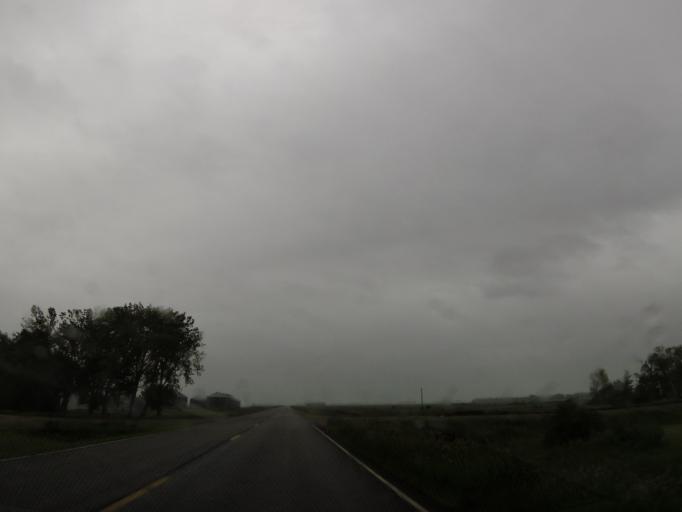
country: US
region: North Dakota
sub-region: Walsh County
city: Grafton
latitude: 48.4702
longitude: -97.4054
